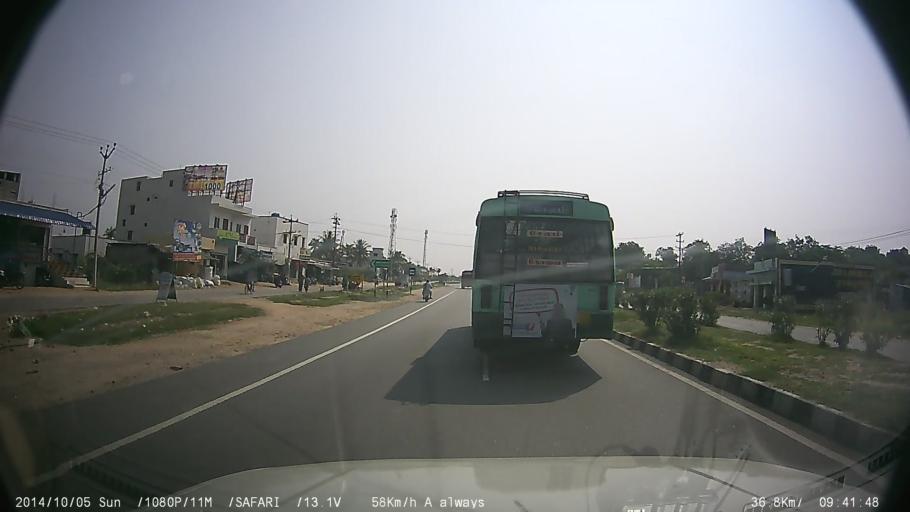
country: IN
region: Tamil Nadu
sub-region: Erode
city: Bhavani
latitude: 11.4464
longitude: 77.7391
